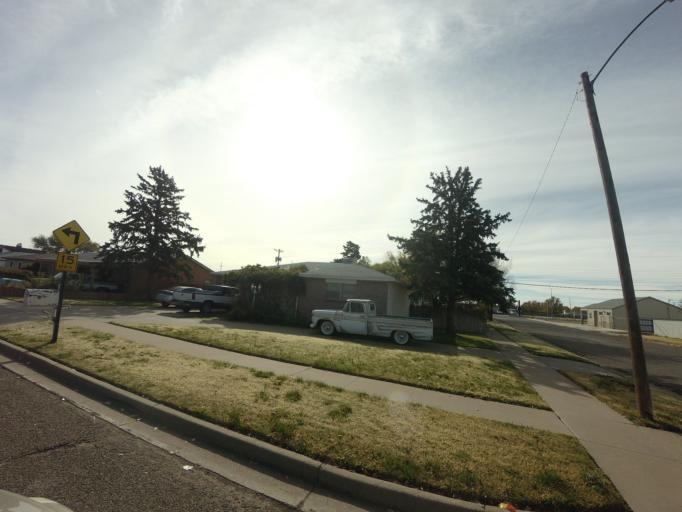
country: US
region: New Mexico
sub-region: Curry County
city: Clovis
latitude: 34.4203
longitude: -103.2273
